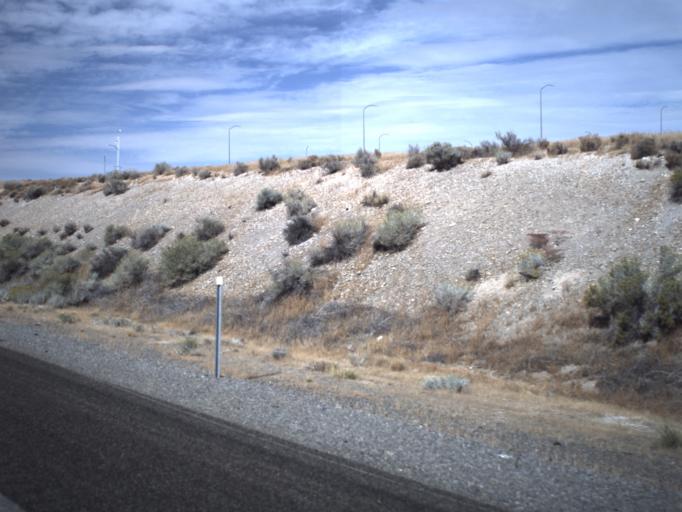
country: US
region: Utah
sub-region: Tooele County
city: Grantsville
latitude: 40.7615
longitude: -113.0082
